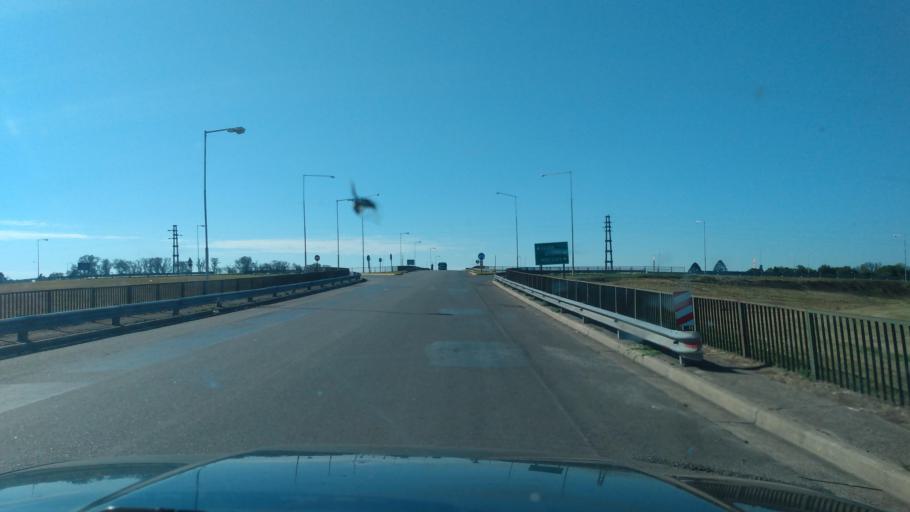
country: AR
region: Buenos Aires
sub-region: Partido de Lujan
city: Lujan
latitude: -34.6064
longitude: -59.1730
